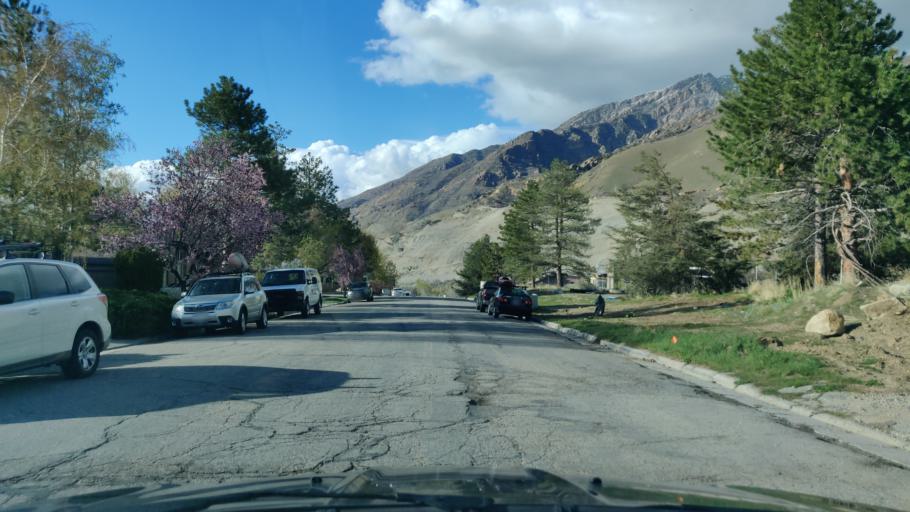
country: US
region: Utah
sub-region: Salt Lake County
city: Cottonwood Heights
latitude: 40.6171
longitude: -111.7918
